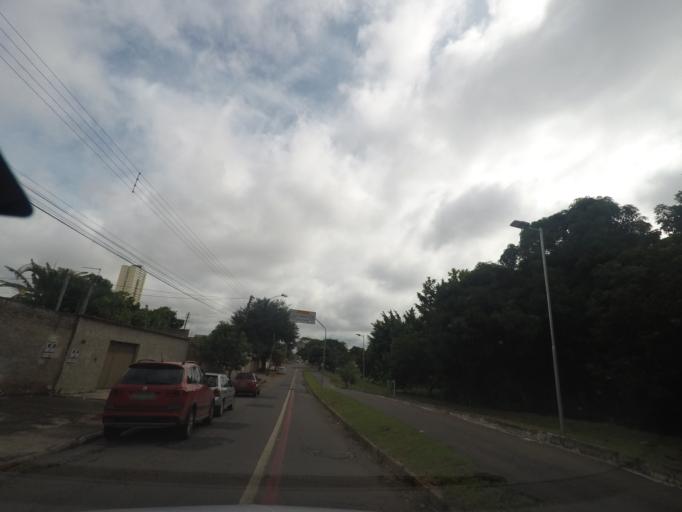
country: BR
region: Goias
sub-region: Goiania
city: Goiania
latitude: -16.7279
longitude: -49.2597
